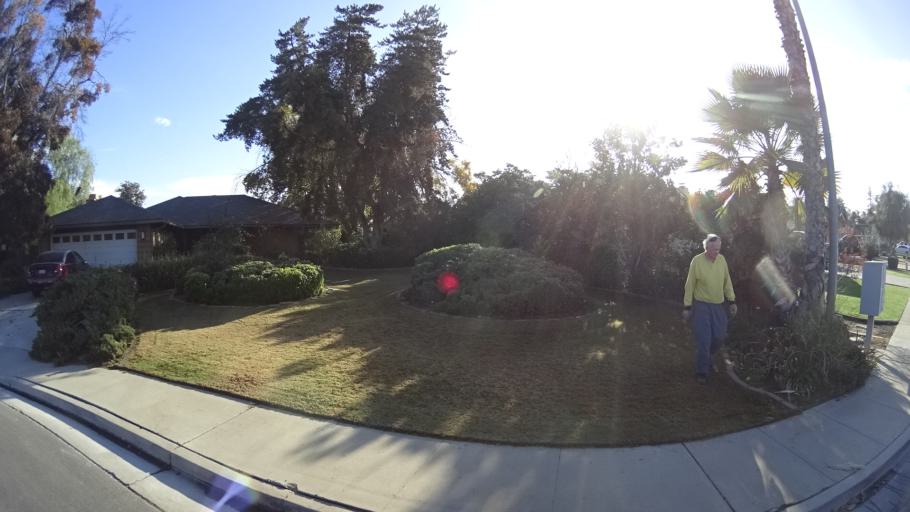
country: US
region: California
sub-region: Kern County
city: Rosedale
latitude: 35.3537
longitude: -119.1537
